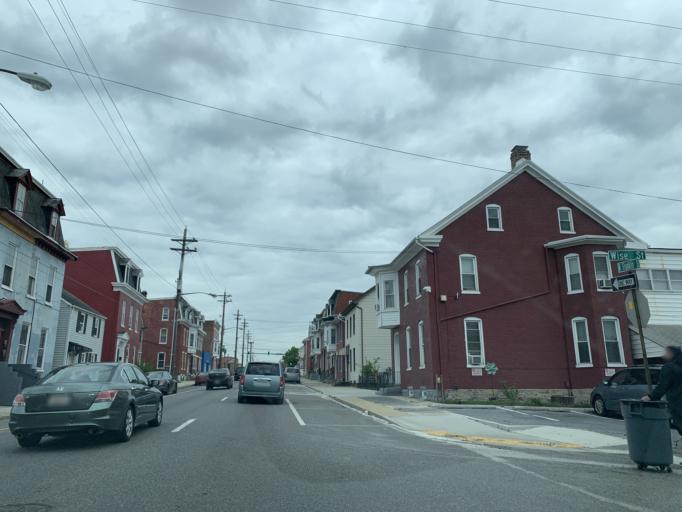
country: US
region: Maryland
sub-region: Washington County
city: Hagerstown
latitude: 39.6479
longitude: -77.7288
